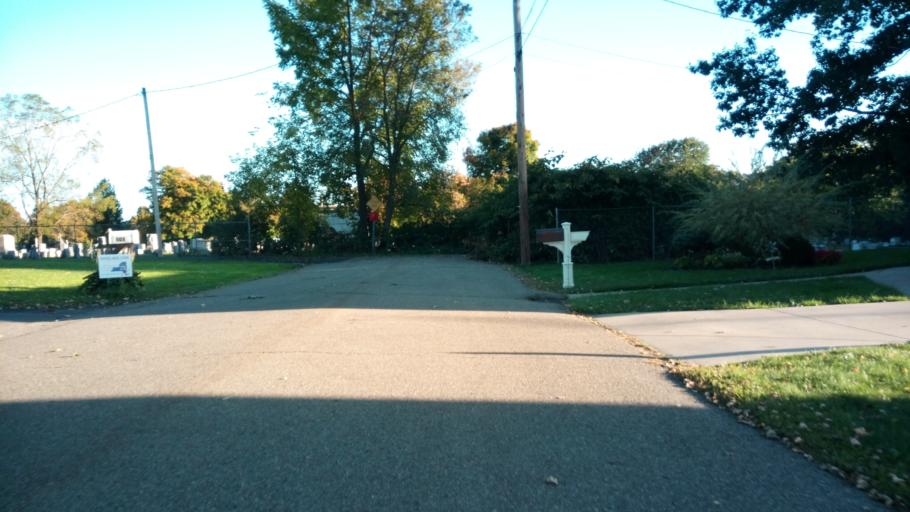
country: US
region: New York
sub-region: Chemung County
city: Southport
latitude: 42.0732
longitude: -76.8189
